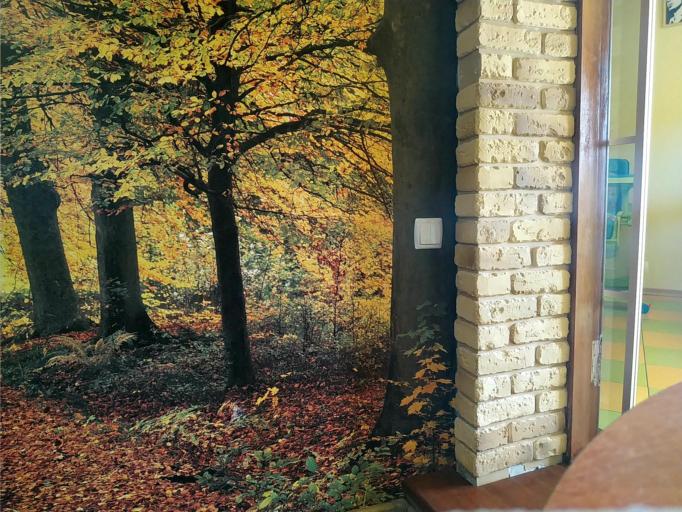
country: RU
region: Smolensk
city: Katyn'
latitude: 54.9743
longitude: 31.7330
